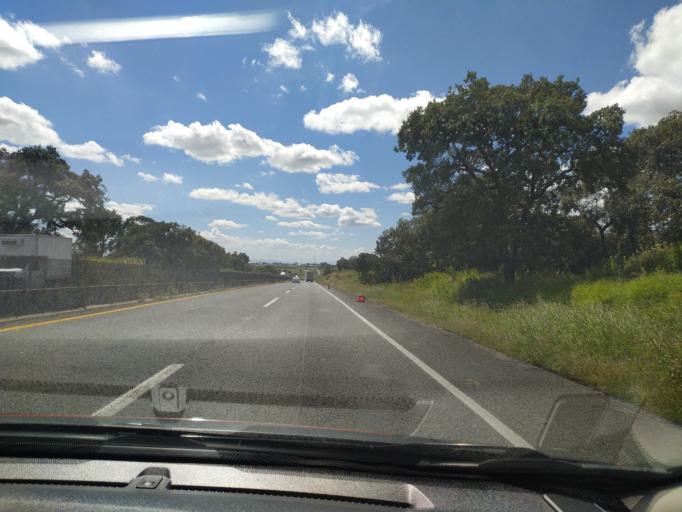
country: MX
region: Jalisco
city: Tepatitlan de Morelos
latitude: 20.8561
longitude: -102.7711
